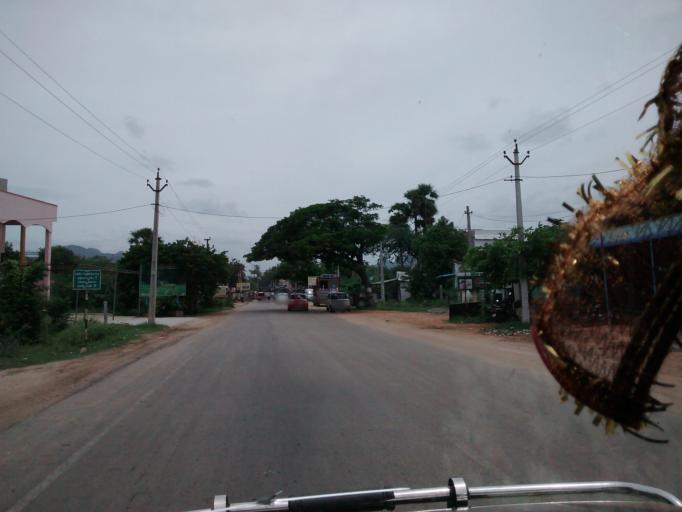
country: IN
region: Andhra Pradesh
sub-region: Chittoor
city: Narasingapuram
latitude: 13.6109
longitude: 79.3305
